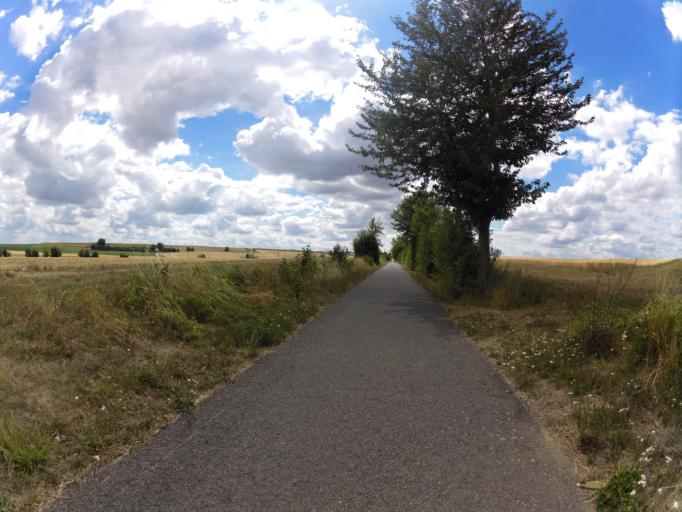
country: DE
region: Bavaria
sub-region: Regierungsbezirk Unterfranken
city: Sonderhofen
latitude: 49.6059
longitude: 10.0053
